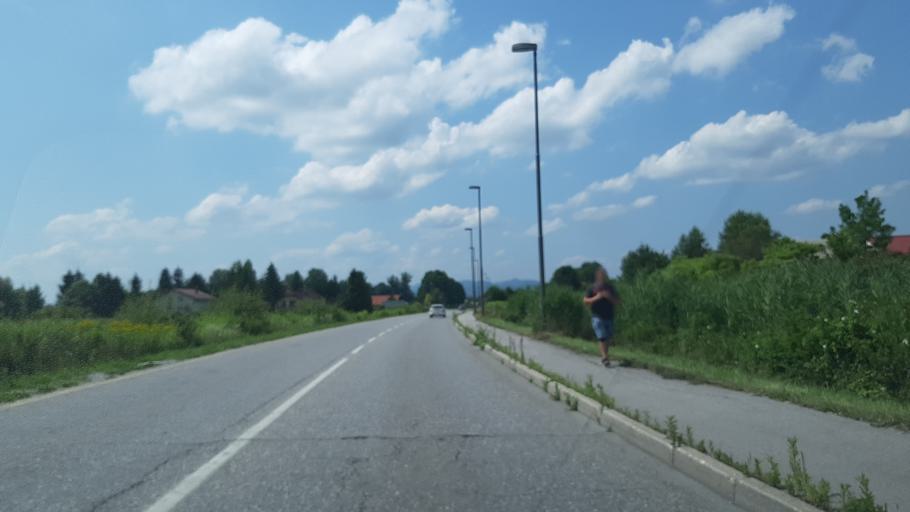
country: SI
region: Ljubljana
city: Ljubljana
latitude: 46.0189
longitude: 14.5244
